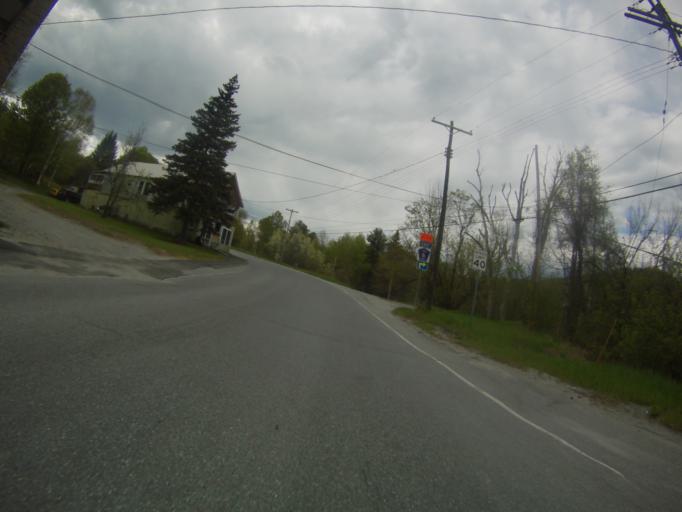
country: US
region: New York
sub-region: Essex County
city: Mineville
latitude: 44.0876
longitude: -73.5335
